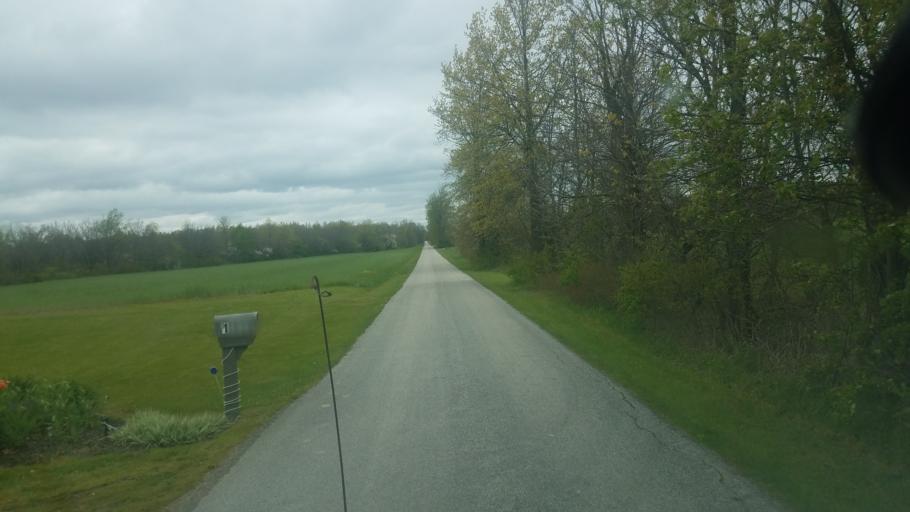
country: US
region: Ohio
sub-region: Marion County
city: Marion
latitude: 40.6240
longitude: -83.2790
